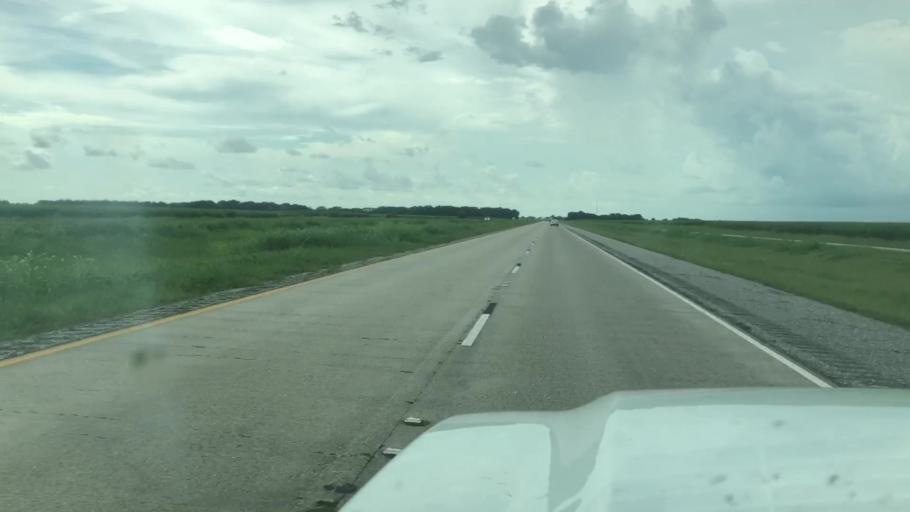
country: US
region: Louisiana
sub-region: Saint Mary Parish
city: Baldwin
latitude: 29.8499
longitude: -91.5955
